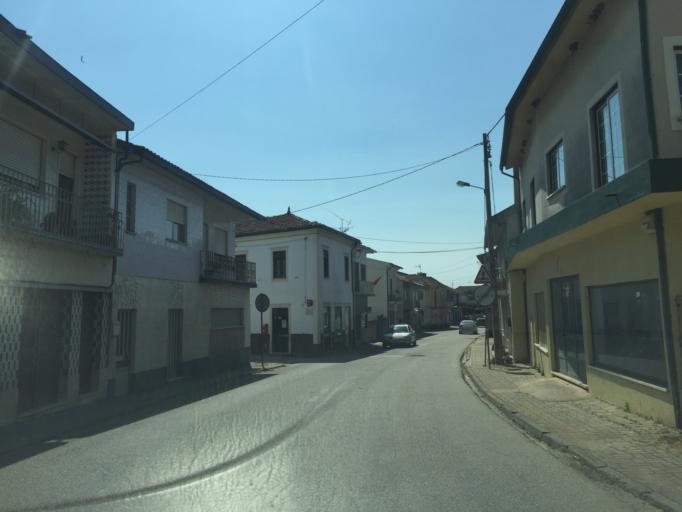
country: PT
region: Aveiro
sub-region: Mealhada
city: Mealhada
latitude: 40.3615
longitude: -8.5023
